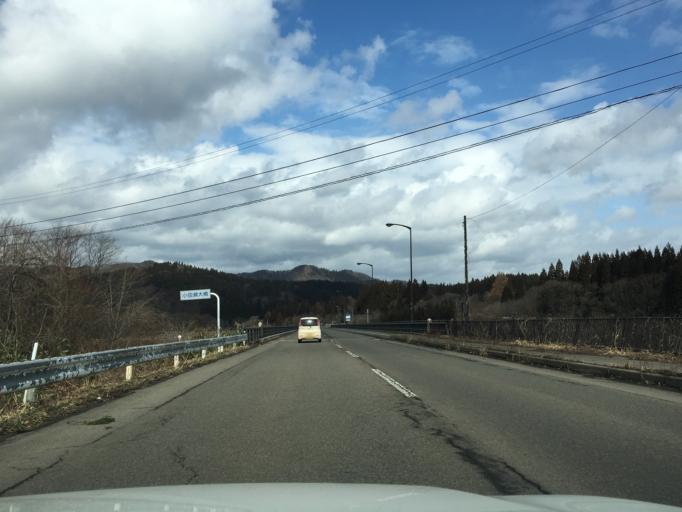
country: JP
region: Akita
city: Takanosu
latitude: 40.0236
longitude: 140.2744
